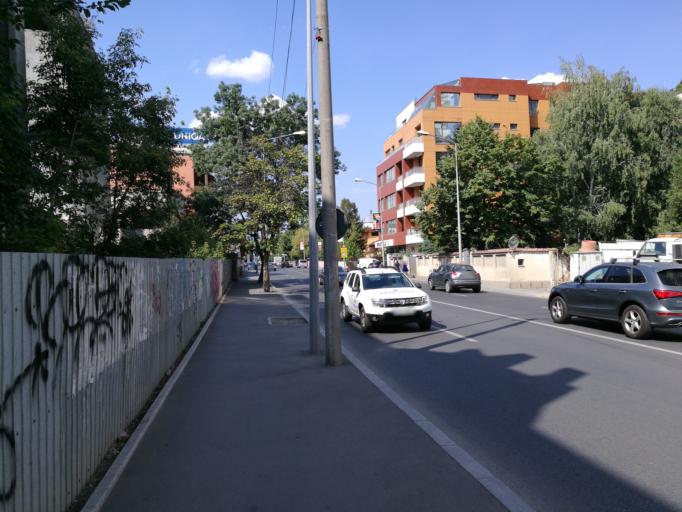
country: RO
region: Bucuresti
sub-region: Municipiul Bucuresti
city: Bucharest
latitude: 44.4770
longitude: 26.0926
